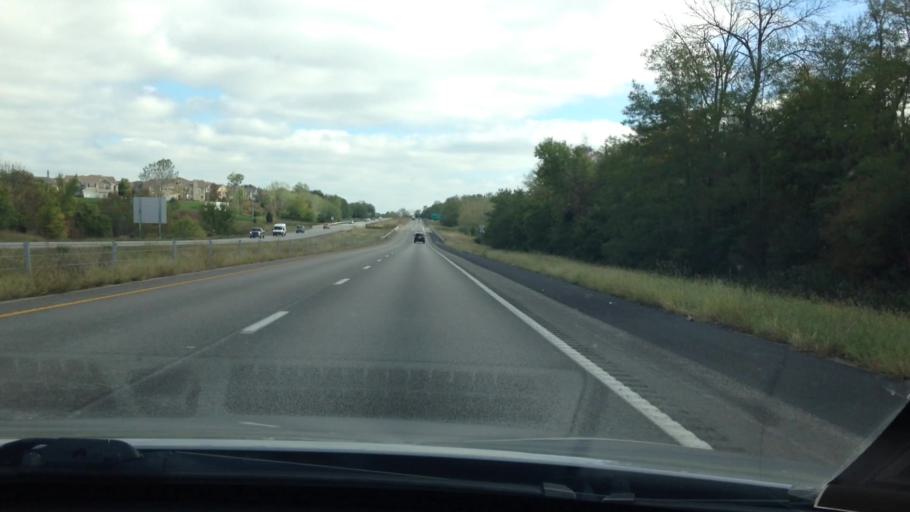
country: US
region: Missouri
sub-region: Platte County
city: Weatherby Lake
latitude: 39.2540
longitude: -94.6211
